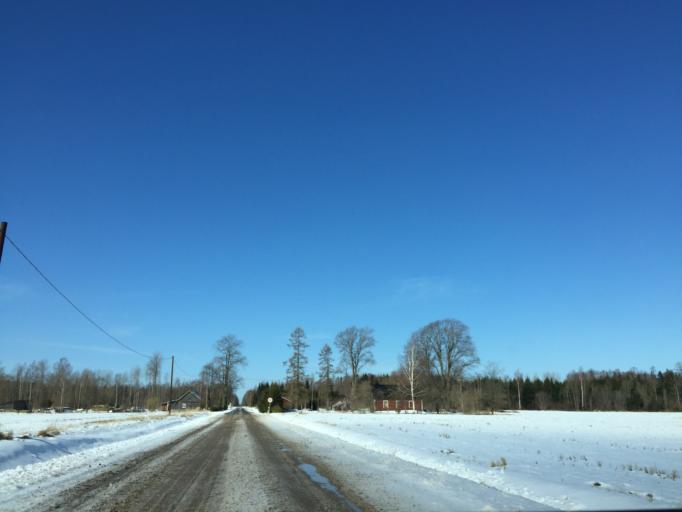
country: LV
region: Aloja
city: Staicele
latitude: 58.0269
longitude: 24.5732
